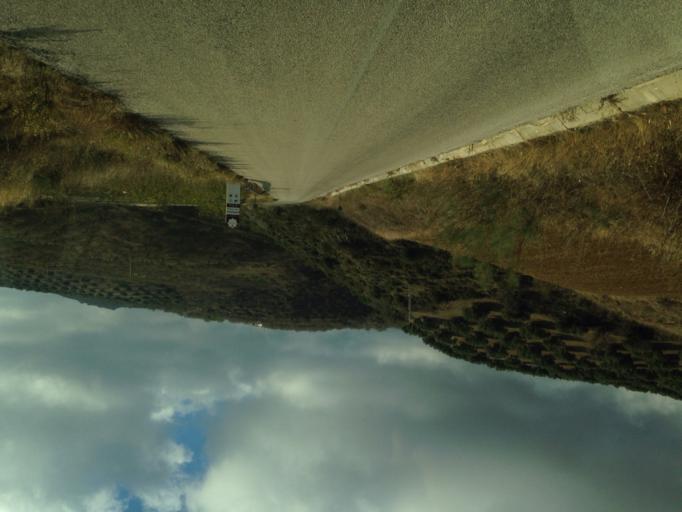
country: ES
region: Andalusia
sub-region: Provincia de Malaga
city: Colmenar
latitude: 36.9339
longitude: -4.3829
